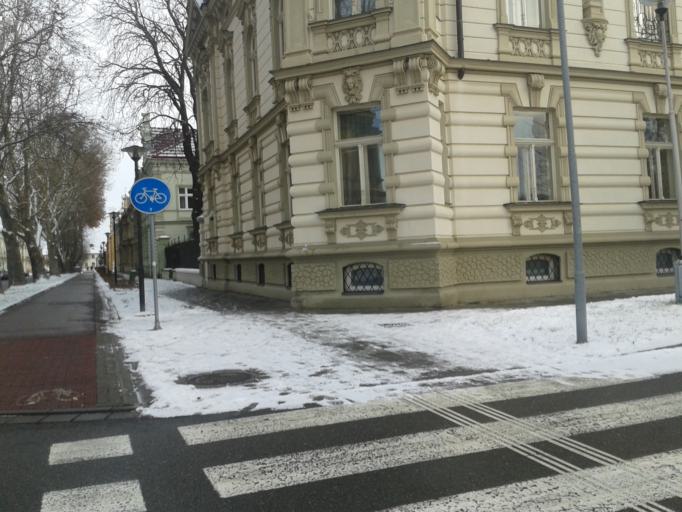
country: CZ
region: Olomoucky
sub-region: Okres Prostejov
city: Prostejov
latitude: 49.4757
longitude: 17.1103
